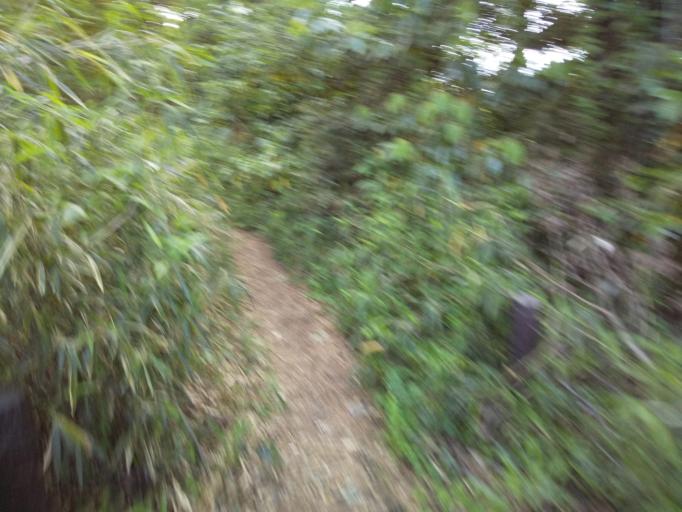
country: JP
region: Kanagawa
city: Zama
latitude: 35.5555
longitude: 139.3673
